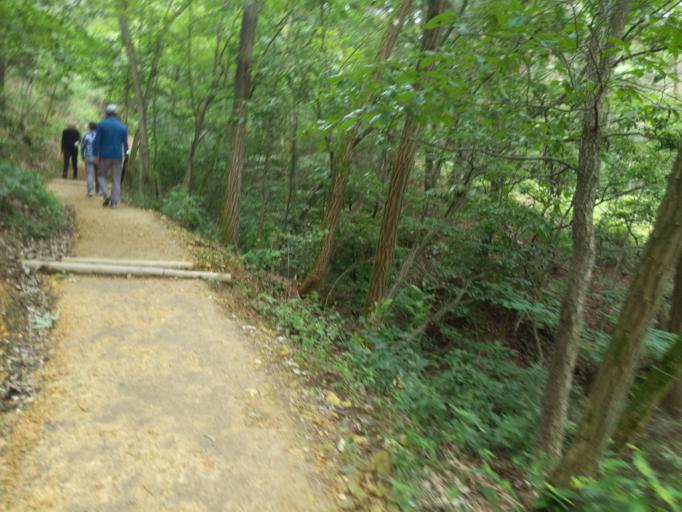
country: KR
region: Daegu
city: Hwawon
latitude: 35.7941
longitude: 128.5260
